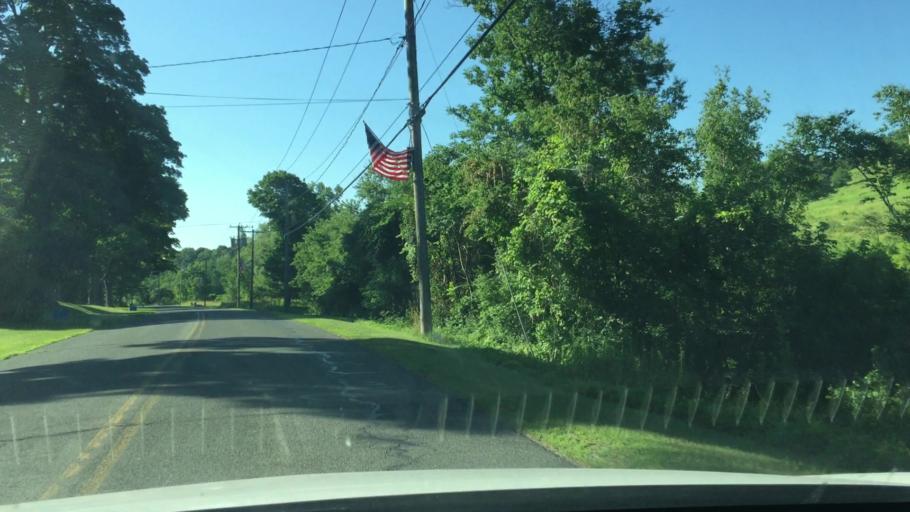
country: US
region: Massachusetts
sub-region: Berkshire County
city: Lee
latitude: 42.2490
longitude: -73.2075
